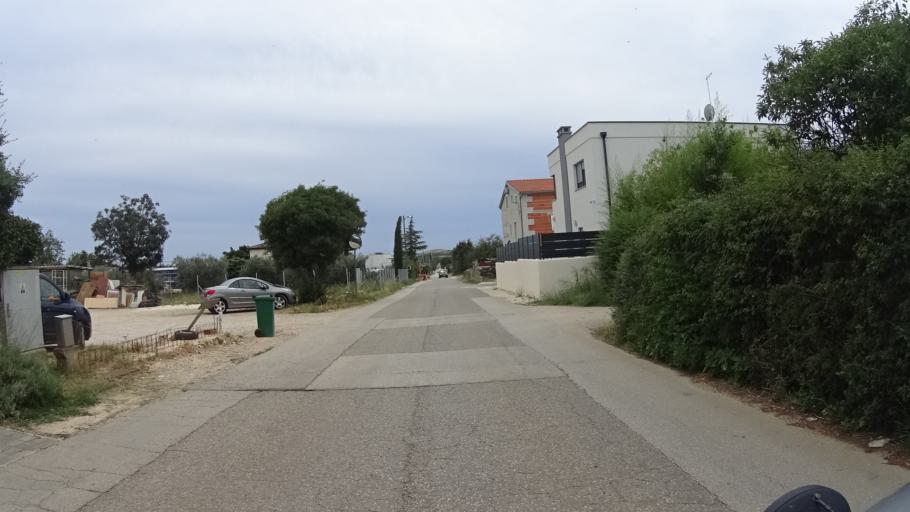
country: HR
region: Istarska
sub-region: Grad Pula
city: Pula
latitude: 44.8605
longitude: 13.8966
